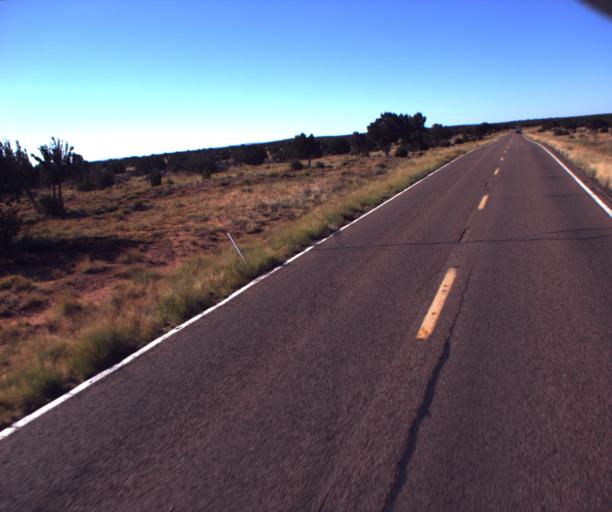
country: US
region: Arizona
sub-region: Navajo County
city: Heber-Overgaard
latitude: 34.5296
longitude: -110.4259
